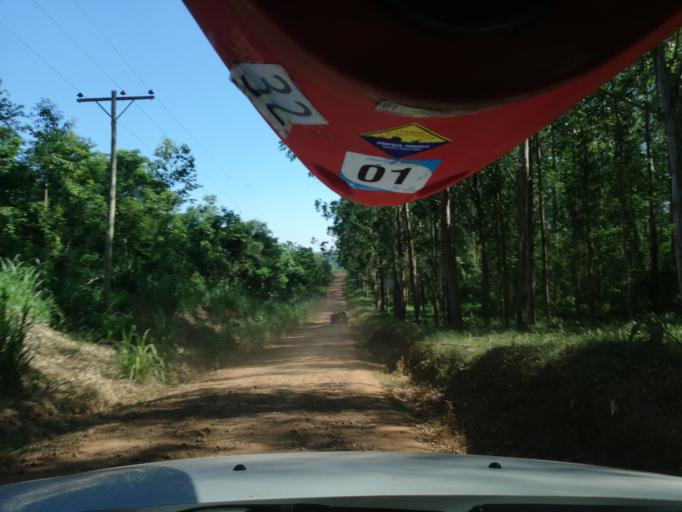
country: AR
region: Misiones
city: Puerto Leoni
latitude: -26.9649
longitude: -55.1525
